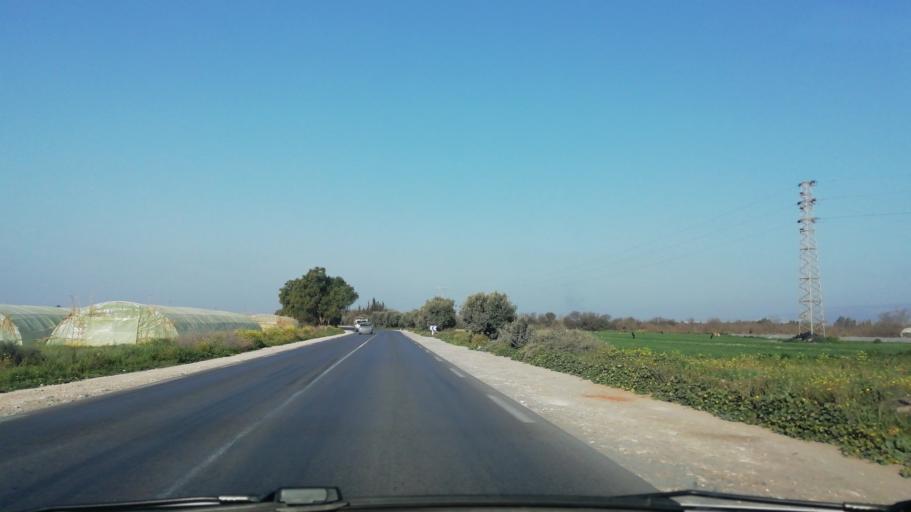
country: DZ
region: Mostaganem
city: Mostaganem
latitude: 35.7566
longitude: 0.1083
